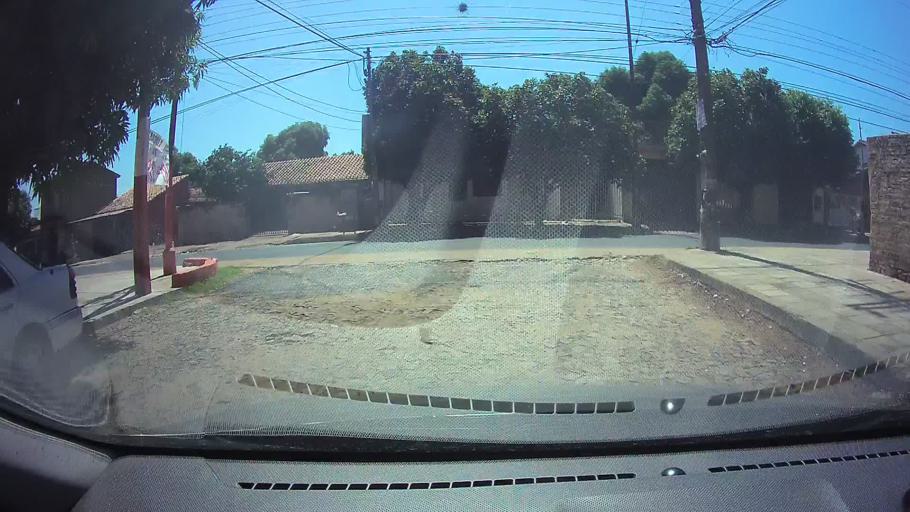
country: PY
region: Central
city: Fernando de la Mora
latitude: -25.3016
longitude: -57.5270
